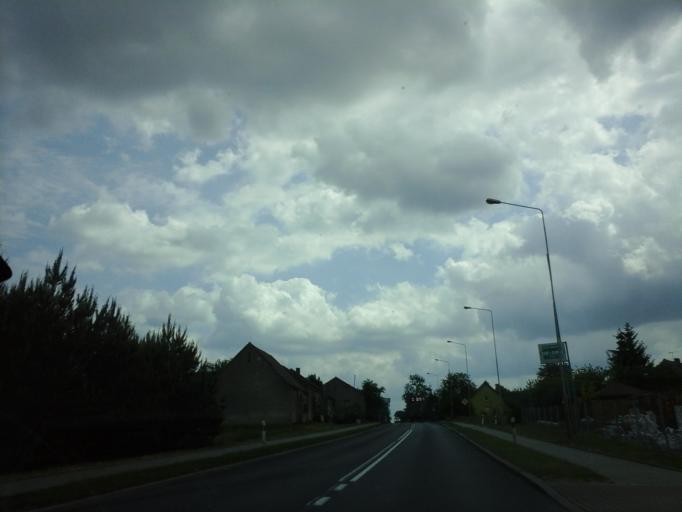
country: PL
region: West Pomeranian Voivodeship
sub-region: Powiat drawski
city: Kalisz Pomorski
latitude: 53.2994
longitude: 15.9181
